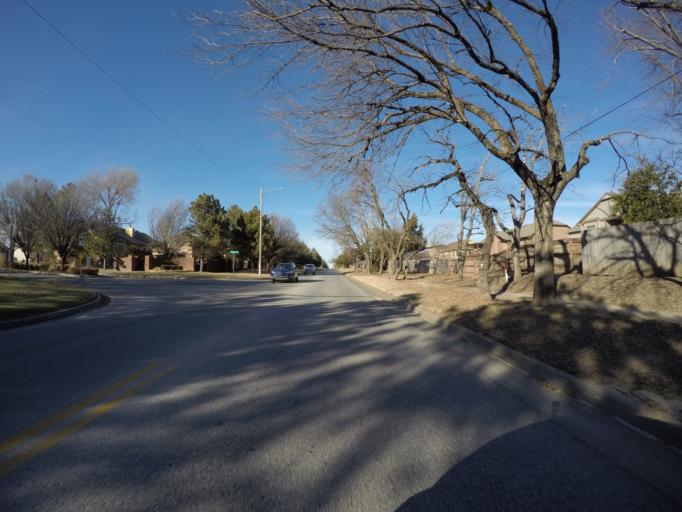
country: US
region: Kansas
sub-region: Sedgwick County
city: Goddard
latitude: 37.6807
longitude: -97.4807
